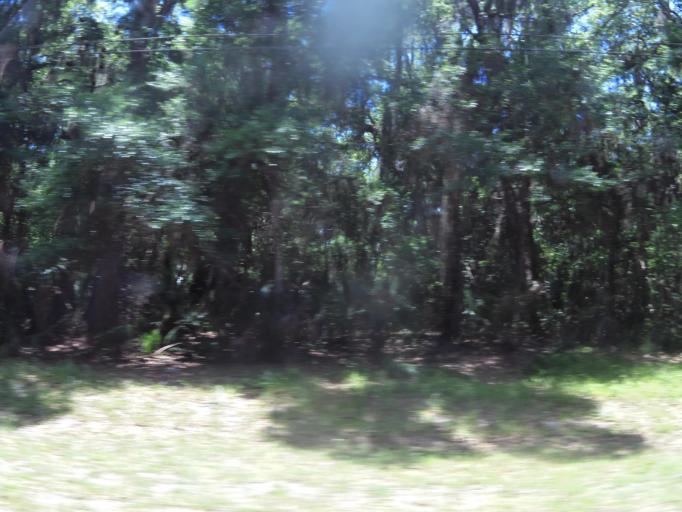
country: US
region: Florida
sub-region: Duval County
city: Atlantic Beach
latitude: 30.4461
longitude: -81.4642
